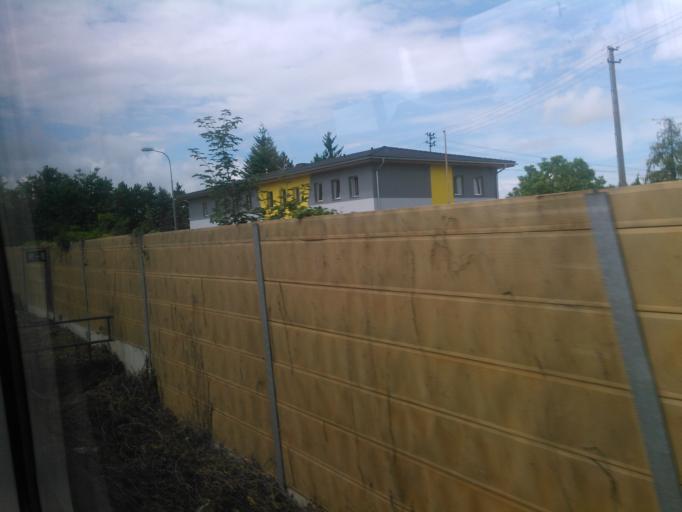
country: AT
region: Upper Austria
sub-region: Wels-Land
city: Holzhausen
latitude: 48.2028
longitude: 14.1026
